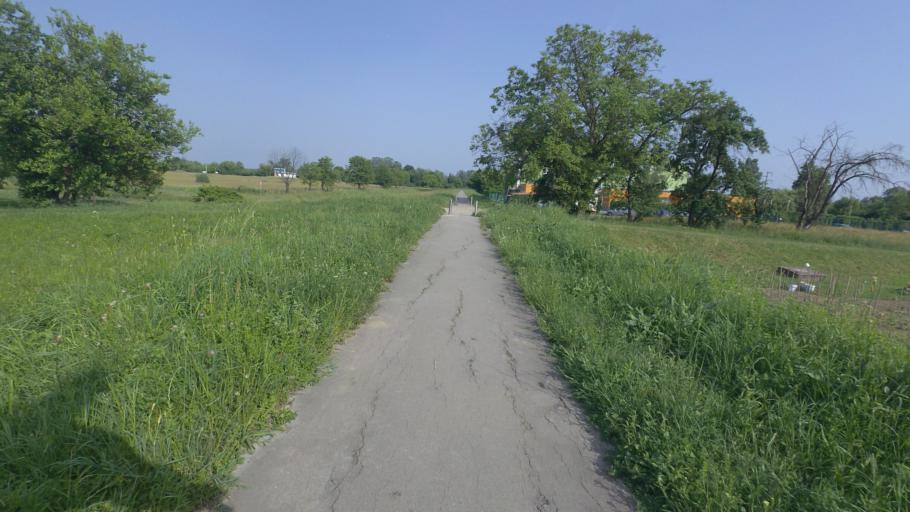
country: HR
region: Karlovacka
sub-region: Grad Karlovac
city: Karlovac
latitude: 45.5024
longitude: 15.5621
